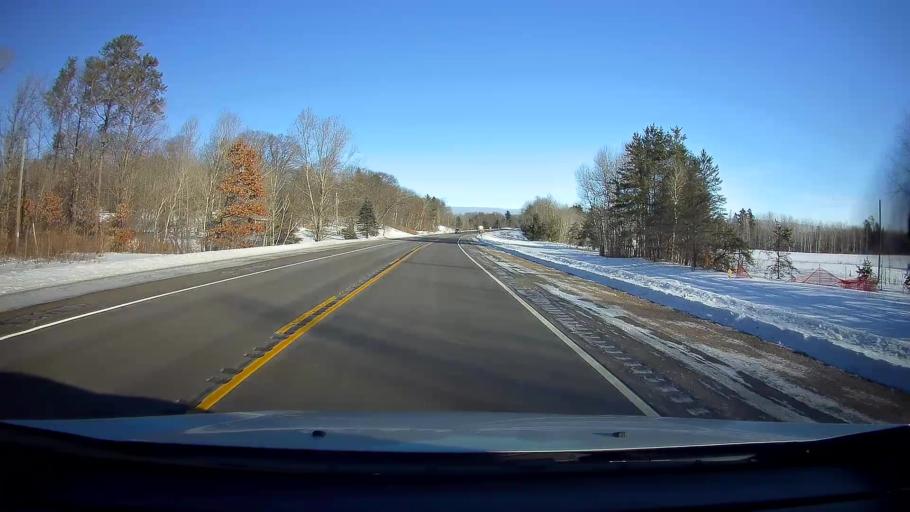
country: US
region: Wisconsin
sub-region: Sawyer County
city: Hayward
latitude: 46.0588
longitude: -91.4403
